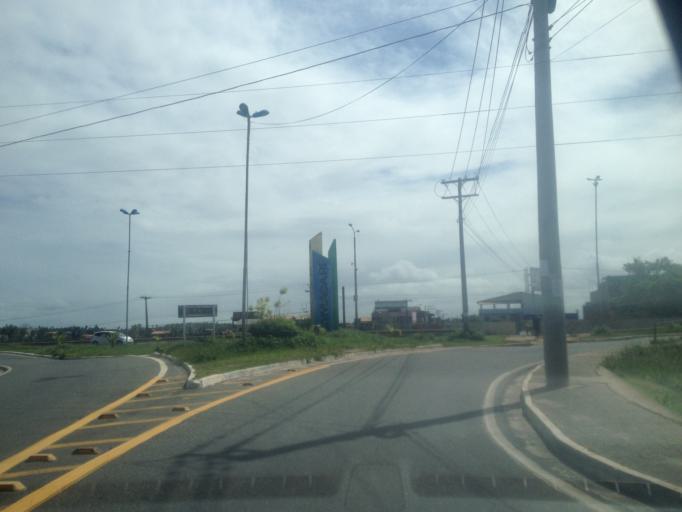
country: BR
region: Bahia
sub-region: Camacari
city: Camacari
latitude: -12.7673
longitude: -38.1870
